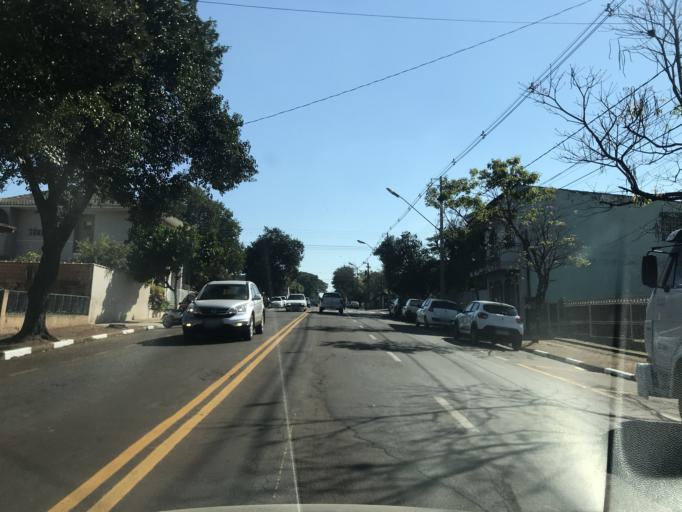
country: BR
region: Parana
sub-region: Toledo
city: Toledo
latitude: -24.7254
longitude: -53.7361
